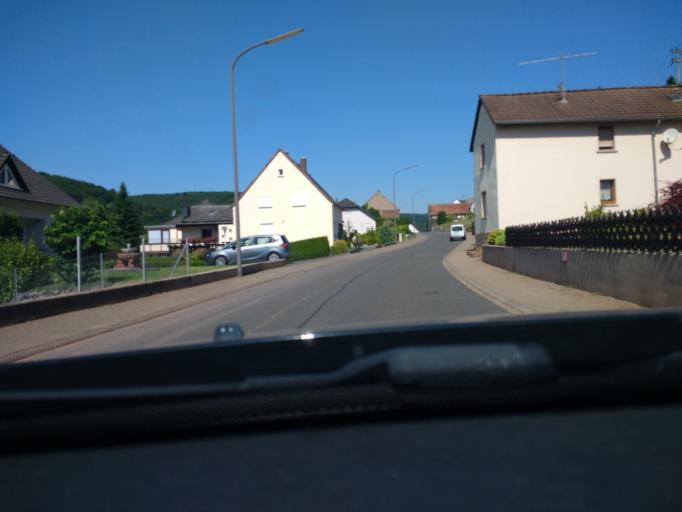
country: DE
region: Rheinland-Pfalz
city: Bausendorf
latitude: 50.0179
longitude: 6.9868
